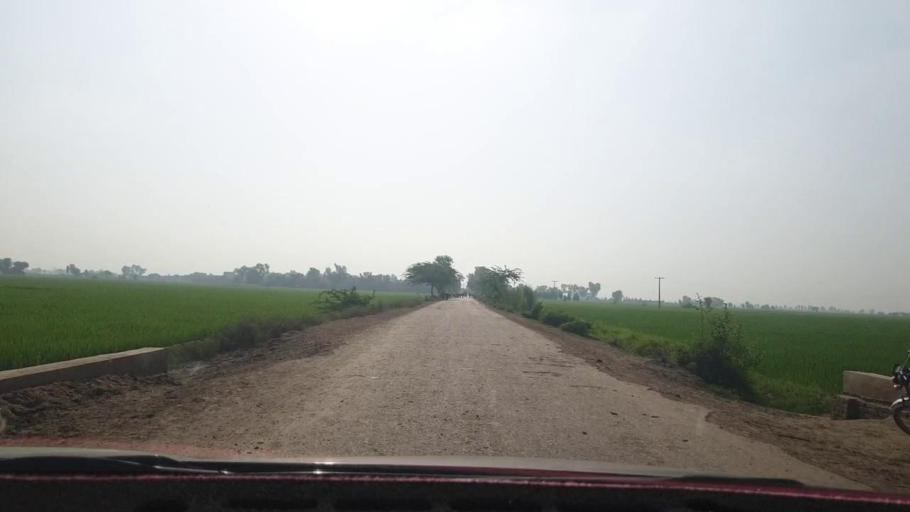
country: PK
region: Sindh
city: Nasirabad
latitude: 27.4410
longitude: 67.9498
